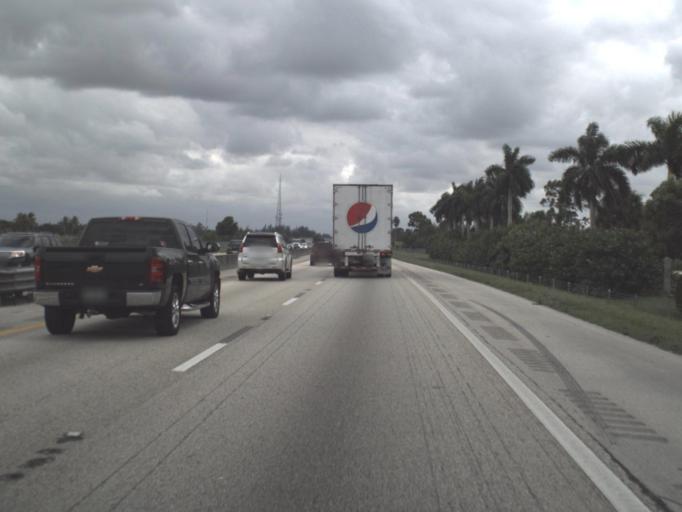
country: US
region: Florida
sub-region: Palm Beach County
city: Lake Belvedere Estates
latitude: 26.6625
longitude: -80.1744
